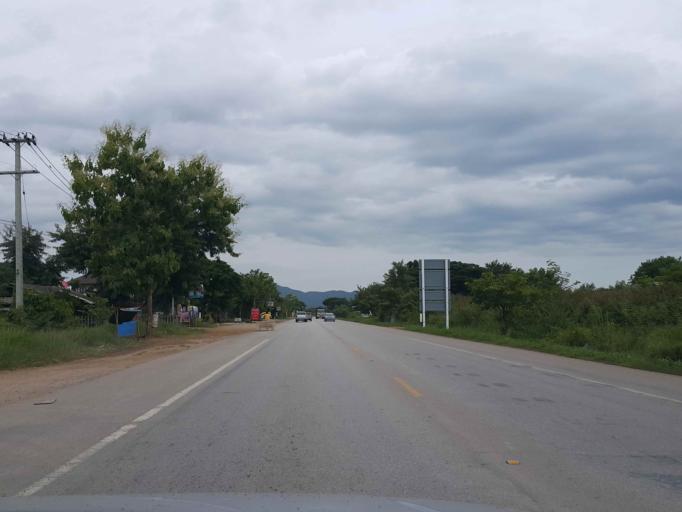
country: TH
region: Lampang
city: Lampang
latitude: 18.2608
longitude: 99.4724
